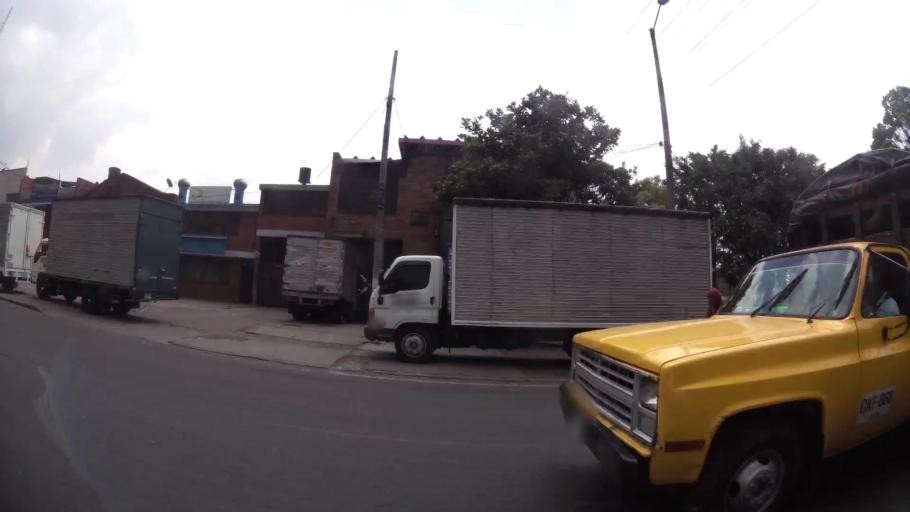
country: CO
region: Bogota D.C.
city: Bogota
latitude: 4.6109
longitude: -74.1033
